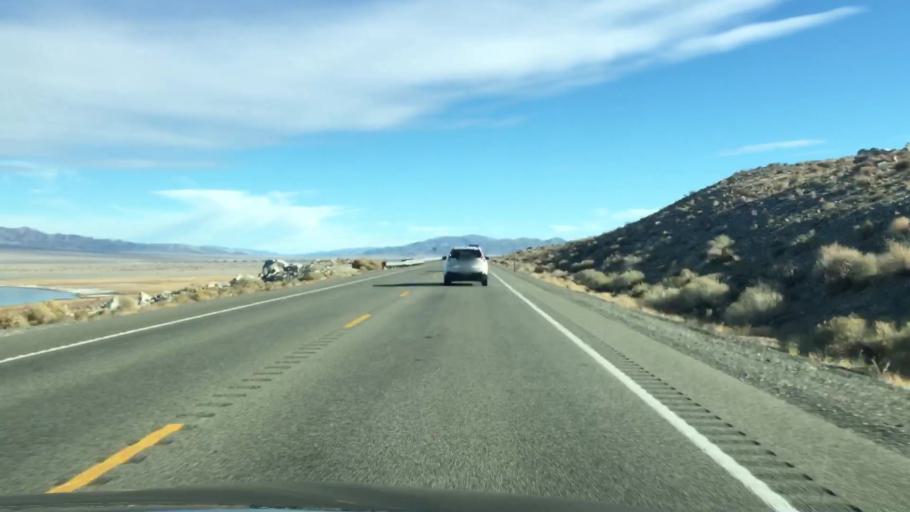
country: US
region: Nevada
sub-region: Mineral County
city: Hawthorne
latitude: 38.6141
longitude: -118.7242
